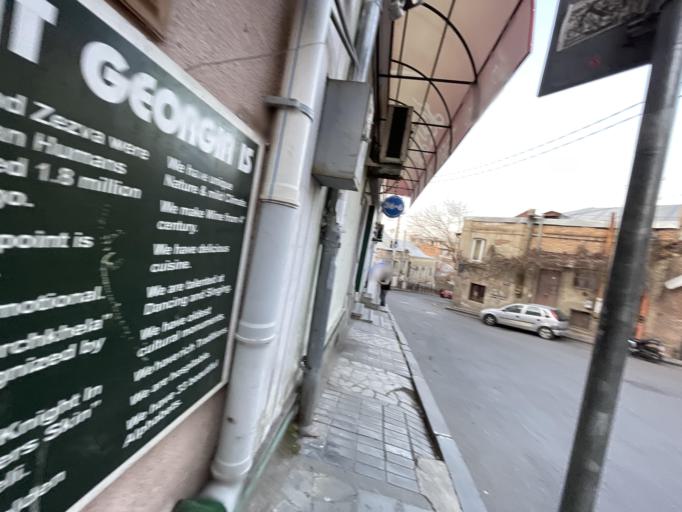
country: GE
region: T'bilisi
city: Tbilisi
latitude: 41.6975
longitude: 44.7947
